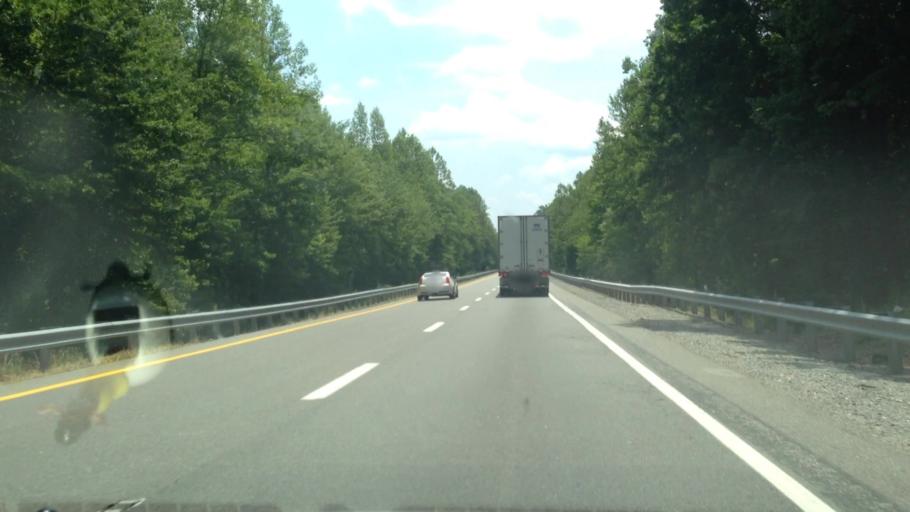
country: US
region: Virginia
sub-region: Henry County
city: Horse Pasture
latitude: 36.6402
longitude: -79.8967
